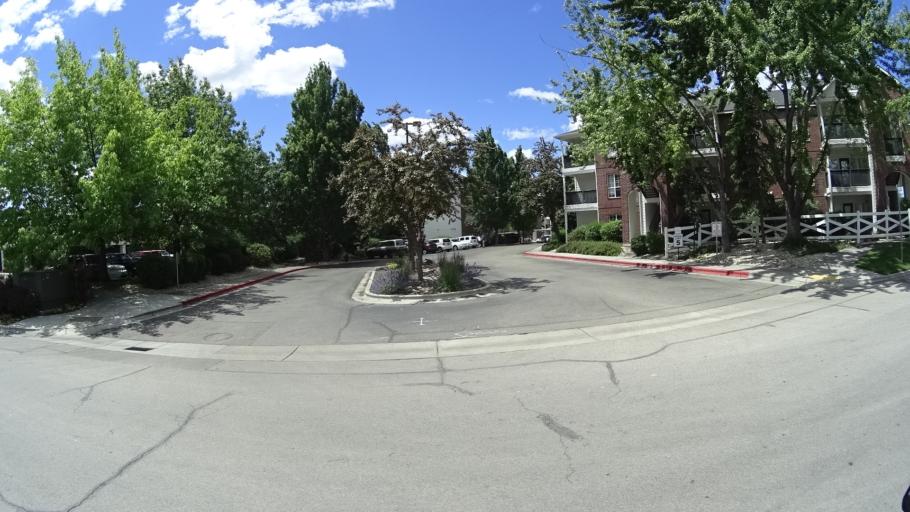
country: US
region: Idaho
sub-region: Ada County
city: Eagle
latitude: 43.6618
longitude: -116.3426
